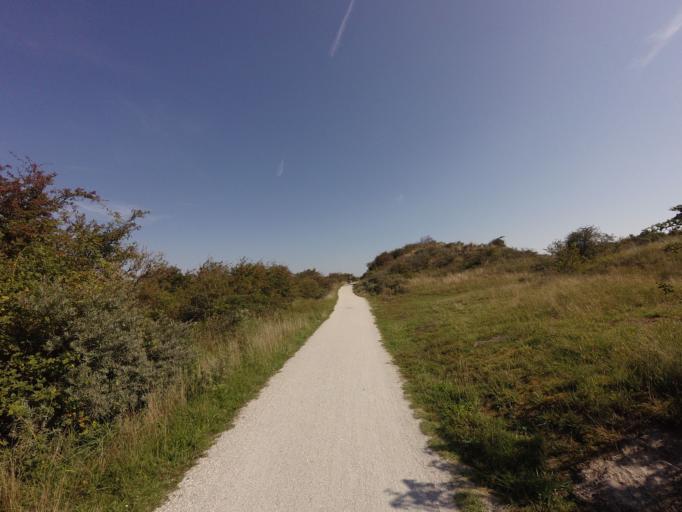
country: NL
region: Friesland
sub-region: Gemeente Schiermonnikoog
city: Schiermonnikoog
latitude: 53.4798
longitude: 6.1451
